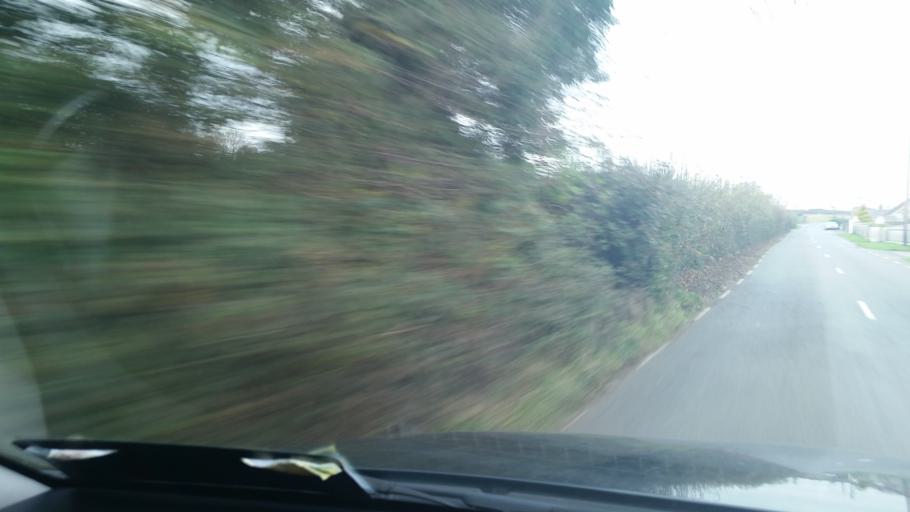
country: IE
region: Leinster
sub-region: Lu
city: Tullyallen
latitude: 53.6969
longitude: -6.4110
